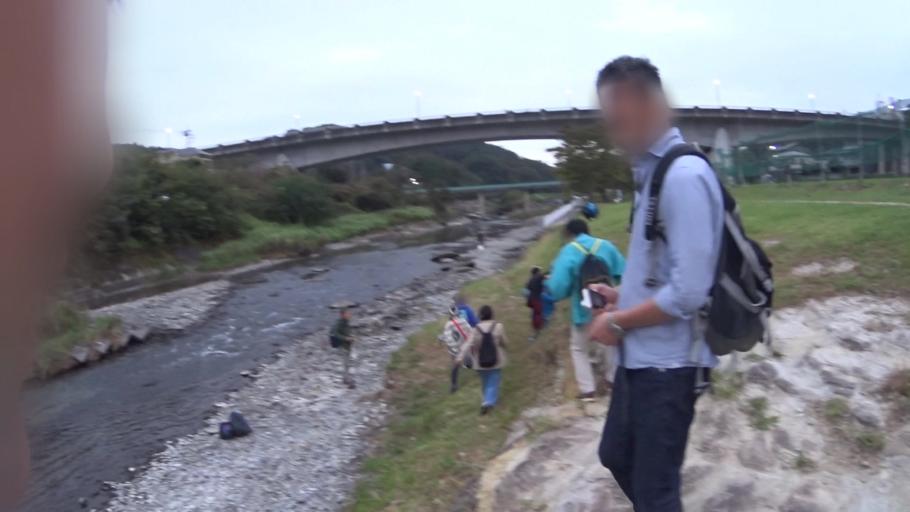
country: JP
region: Saitama
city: Hanno
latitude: 35.8473
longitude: 139.3161
